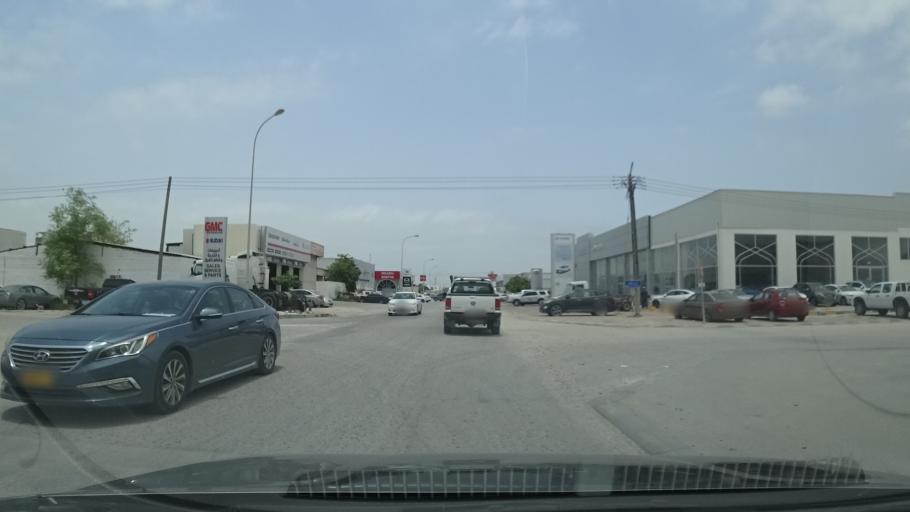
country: OM
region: Zufar
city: Salalah
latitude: 17.0173
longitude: 54.0446
